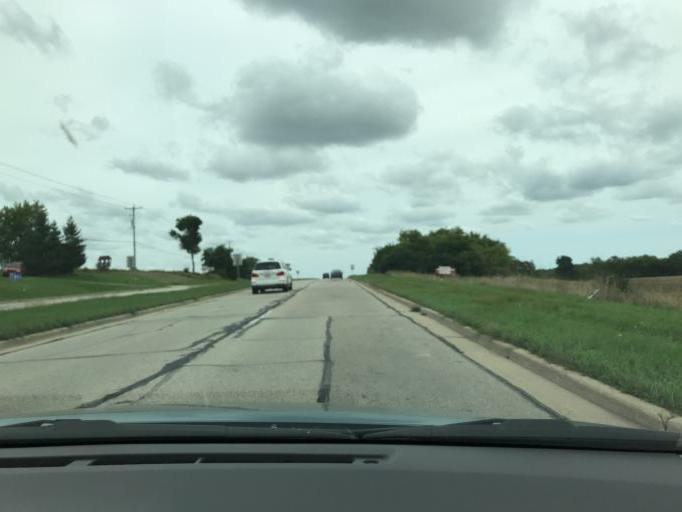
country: US
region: Wisconsin
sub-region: Kenosha County
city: Paddock Lake
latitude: 42.5682
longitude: -88.0946
